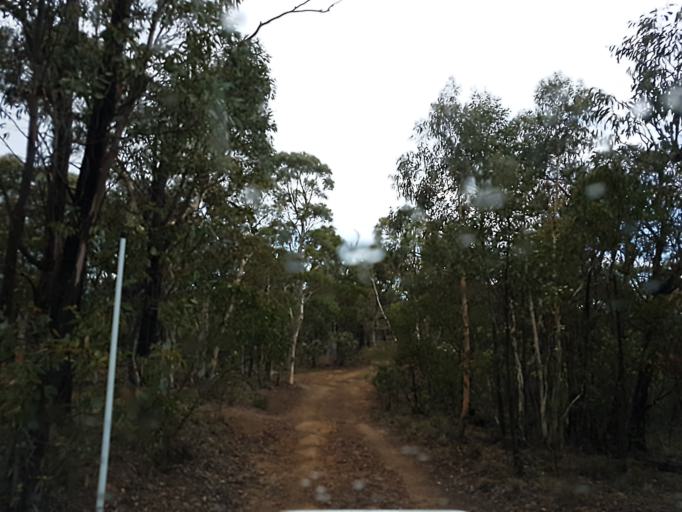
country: AU
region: New South Wales
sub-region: Snowy River
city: Jindabyne
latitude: -36.9031
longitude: 148.3425
